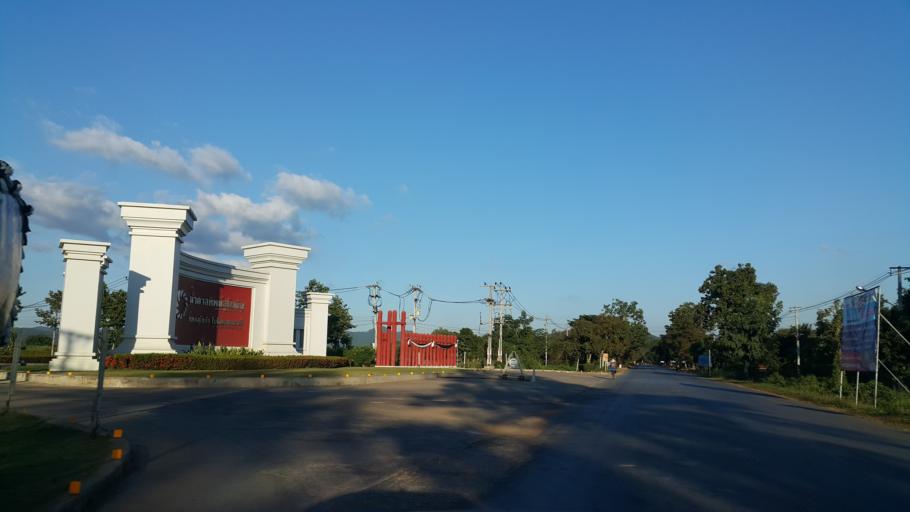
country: TH
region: Sukhothai
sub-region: Amphoe Si Satchanalai
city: Si Satchanalai
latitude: 17.5516
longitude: 99.8665
